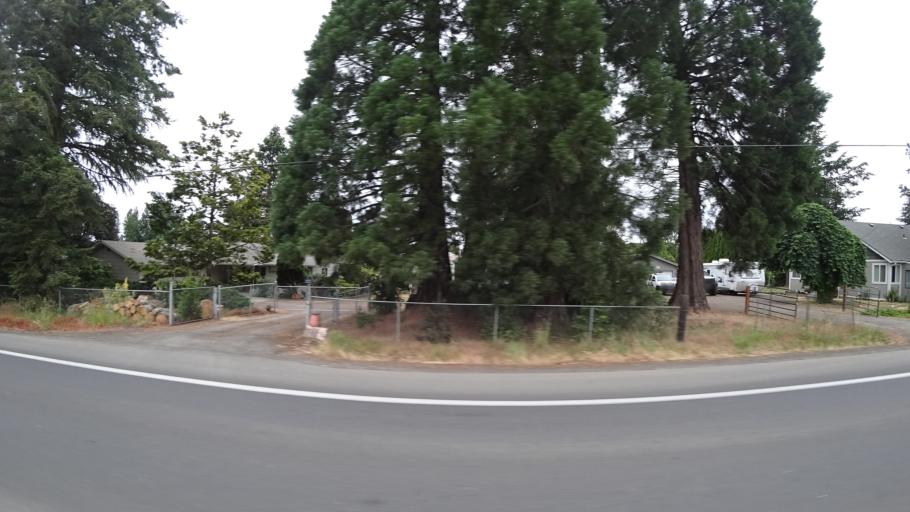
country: US
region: Oregon
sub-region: Washington County
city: Hillsboro
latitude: 45.4880
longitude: -122.9388
